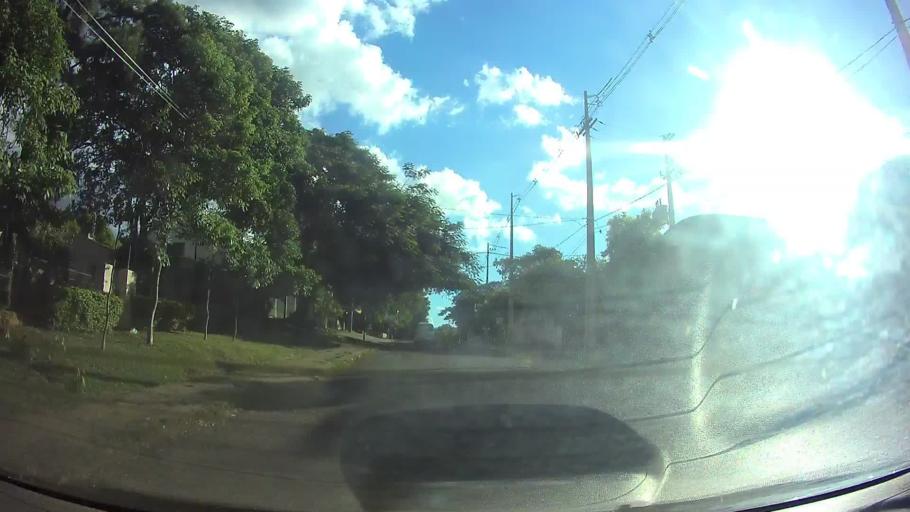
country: PY
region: Cordillera
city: Altos
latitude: -25.2605
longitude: -57.2488
